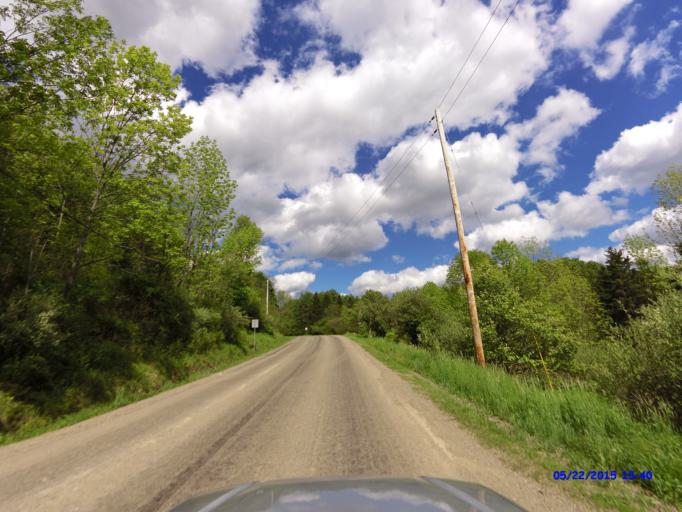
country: US
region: New York
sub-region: Cattaraugus County
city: Franklinville
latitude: 42.3048
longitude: -78.6045
